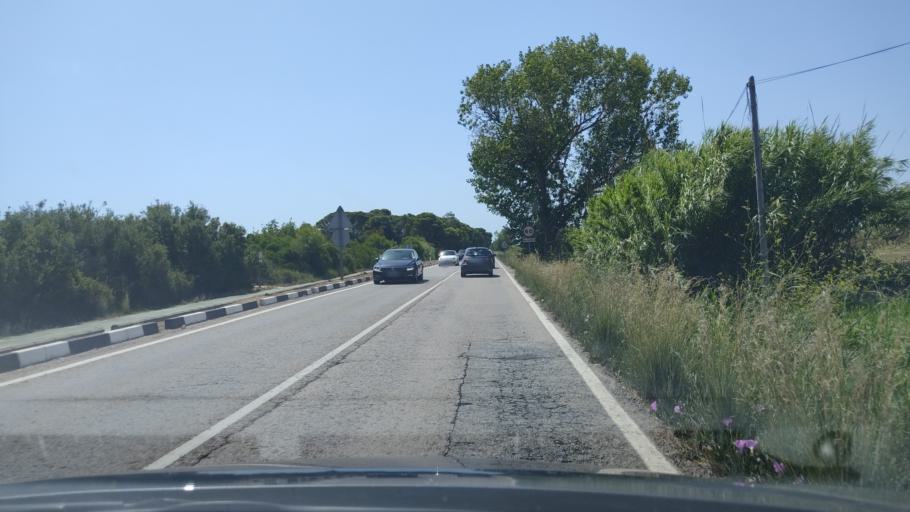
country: ES
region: Valencia
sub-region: Provincia de Valencia
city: Alfafar
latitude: 39.3744
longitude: -0.3310
